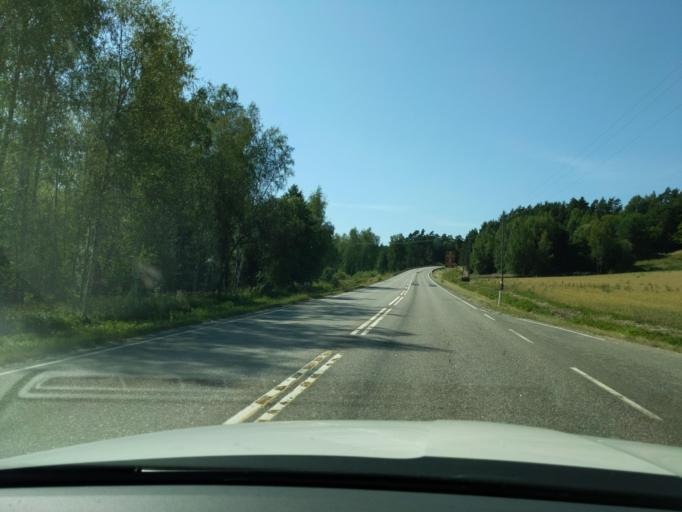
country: FI
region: Uusimaa
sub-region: Raaseporin
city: Ekenaes
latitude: 60.0652
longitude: 23.2877
